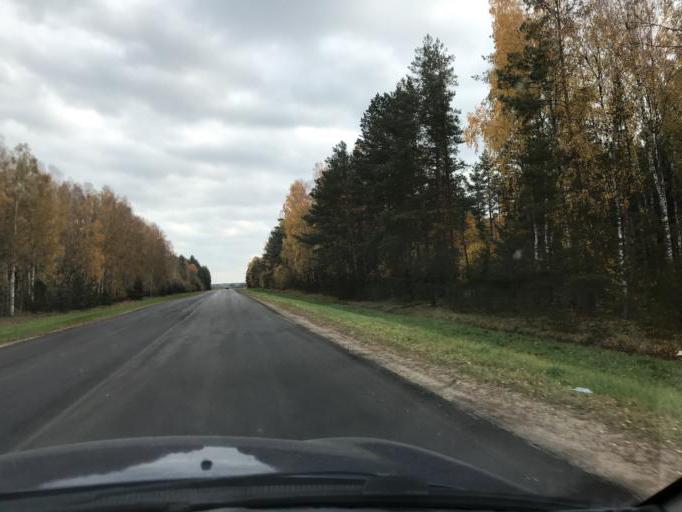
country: BY
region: Grodnenskaya
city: Lida
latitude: 53.7504
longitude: 25.2302
